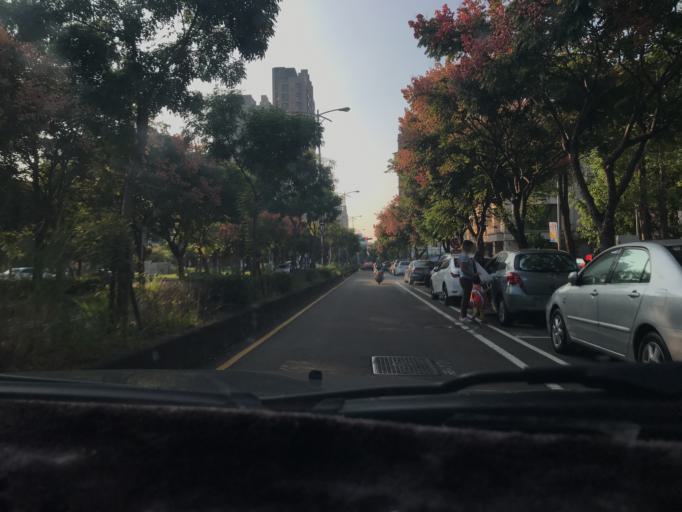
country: TW
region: Taiwan
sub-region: Hsinchu
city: Zhubei
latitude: 24.8058
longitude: 121.0327
